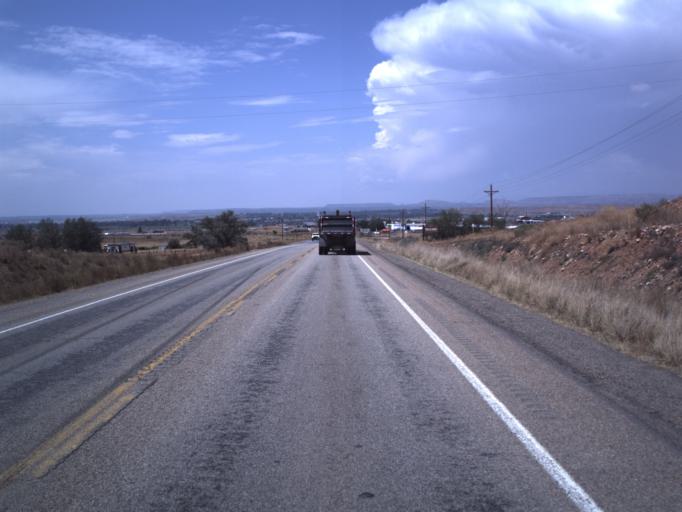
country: US
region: Utah
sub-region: Duchesne County
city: Roosevelt
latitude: 40.3021
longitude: -109.9165
